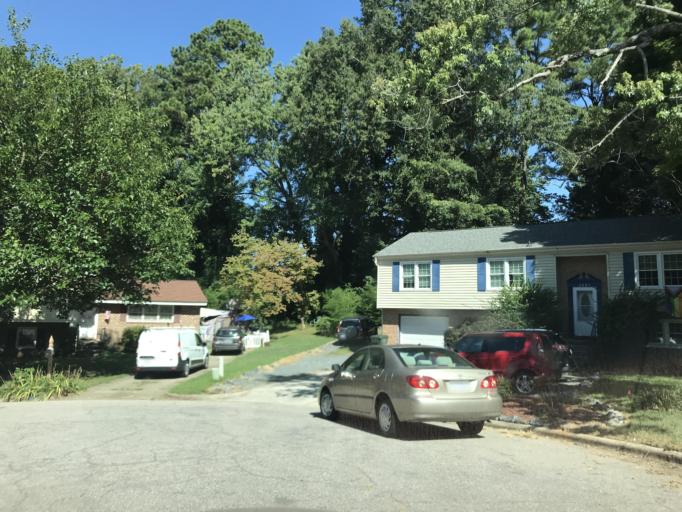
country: US
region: North Carolina
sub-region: Wake County
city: Raleigh
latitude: 35.8348
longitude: -78.5946
